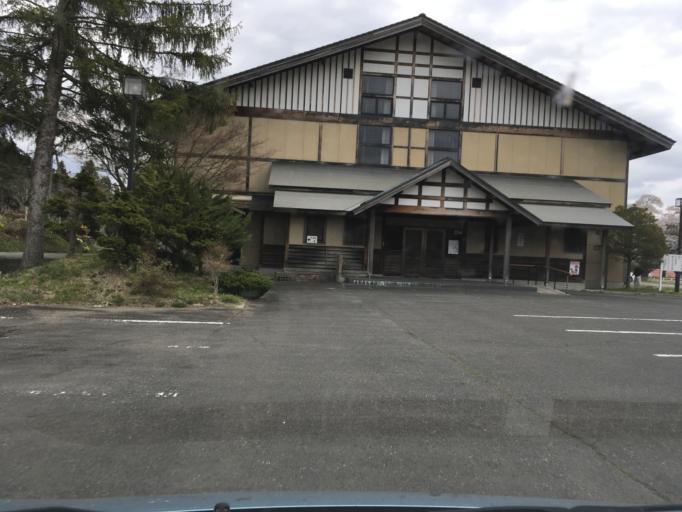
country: JP
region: Iwate
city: Ichinoseki
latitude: 38.9764
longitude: 141.2059
